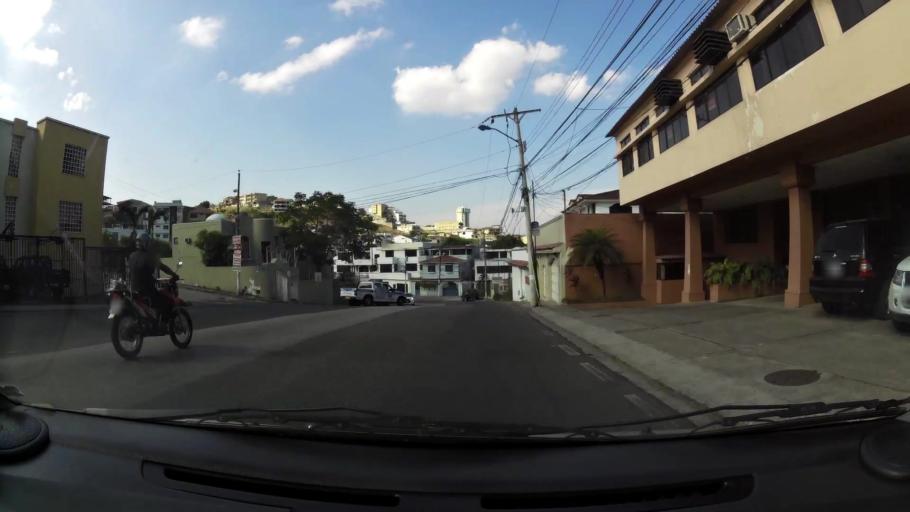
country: EC
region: Guayas
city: Santa Lucia
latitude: -2.1582
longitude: -79.9470
